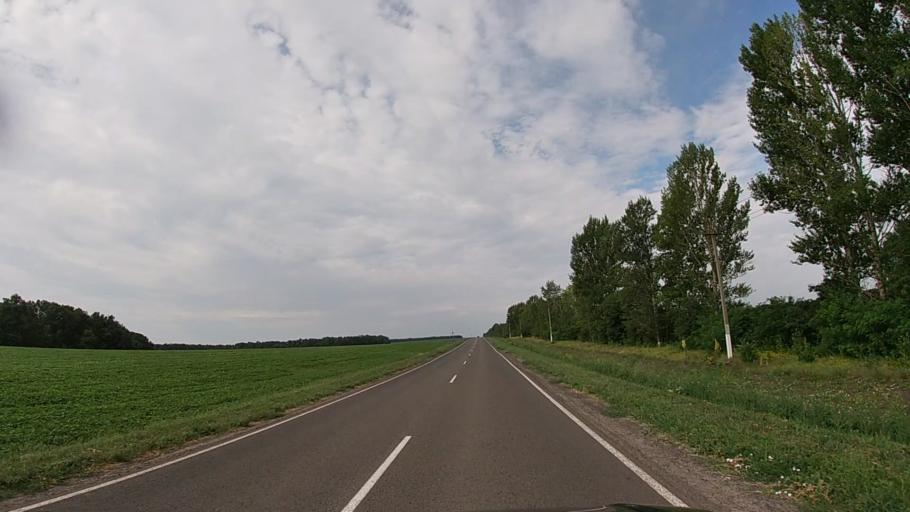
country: RU
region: Belgorod
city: Krasnaya Yaruga
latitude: 50.8315
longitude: 35.4813
